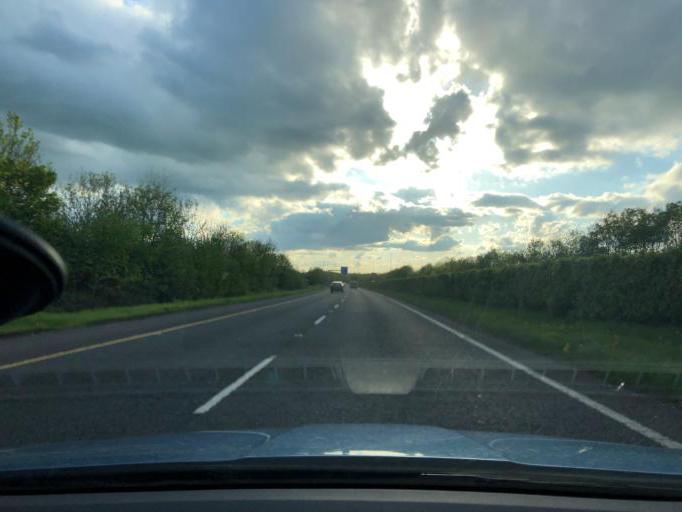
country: IE
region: Leinster
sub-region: Kildare
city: Maynooth
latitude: 53.3663
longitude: -6.5775
